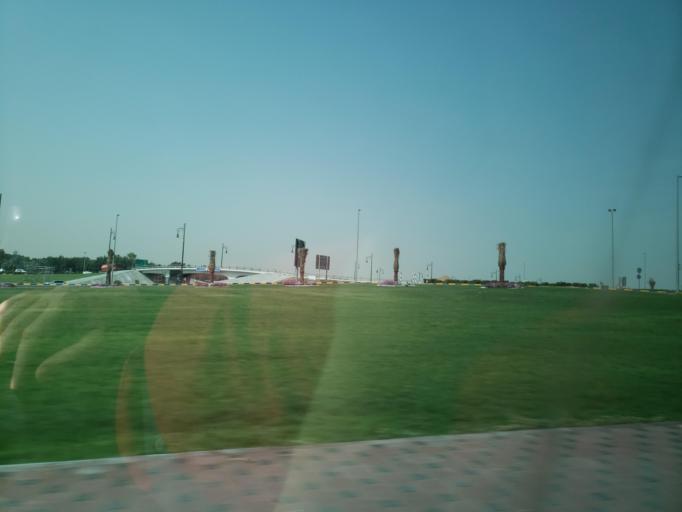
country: AE
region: Ash Shariqah
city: Sharjah
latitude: 25.3079
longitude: 55.5792
